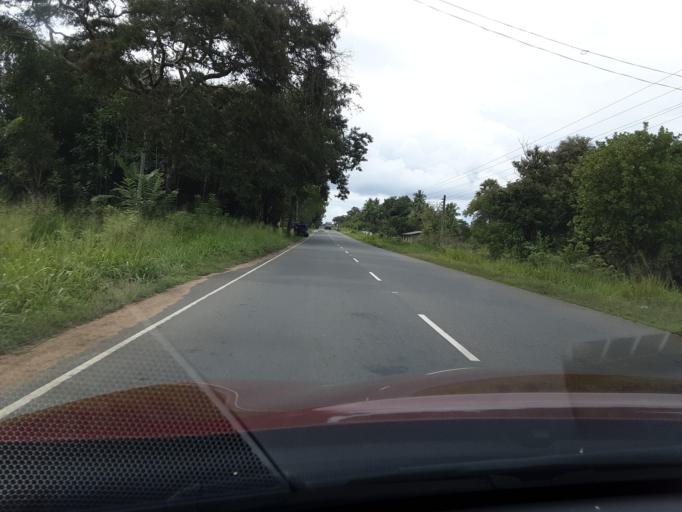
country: LK
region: Uva
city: Badulla
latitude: 7.3929
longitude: 81.1310
